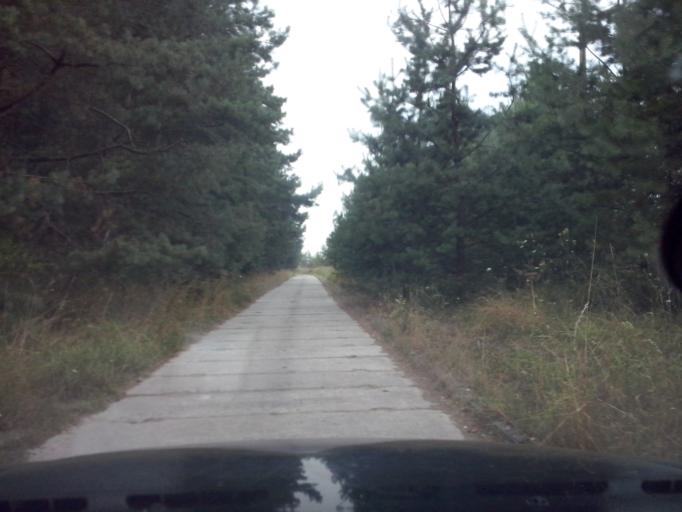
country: PL
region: Swietokrzyskie
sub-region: Powiat kielecki
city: Brzeziny
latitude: 50.7575
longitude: 20.5808
